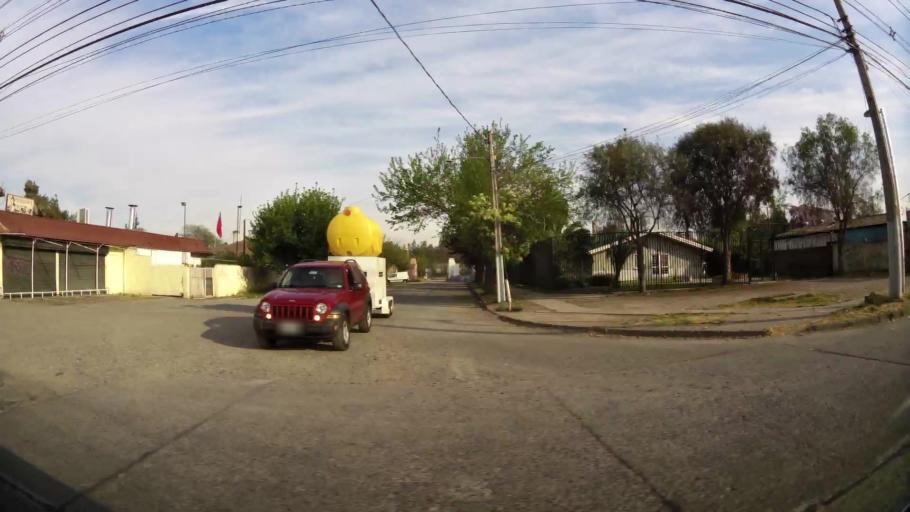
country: CL
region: Santiago Metropolitan
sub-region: Provincia de Talagante
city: Penaflor
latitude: -33.5684
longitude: -70.8145
